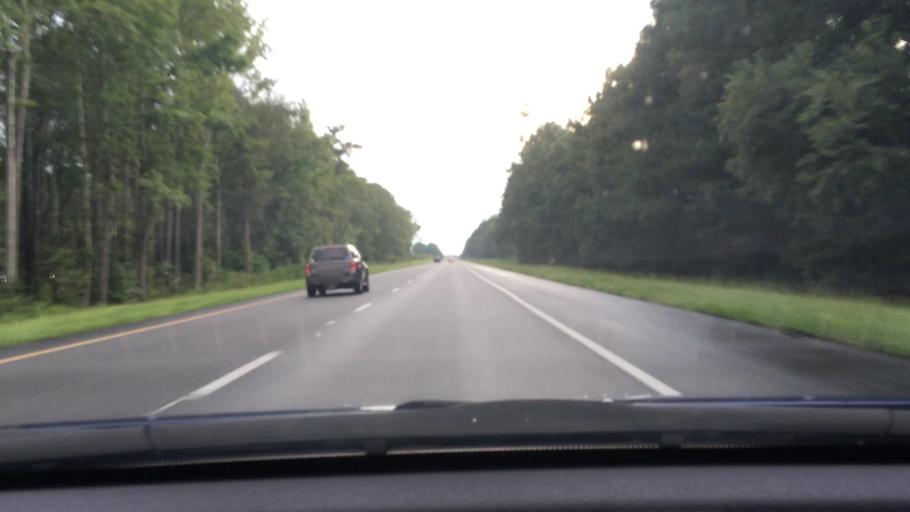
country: US
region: South Carolina
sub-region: Lee County
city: Bishopville
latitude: 34.1960
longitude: -80.2999
